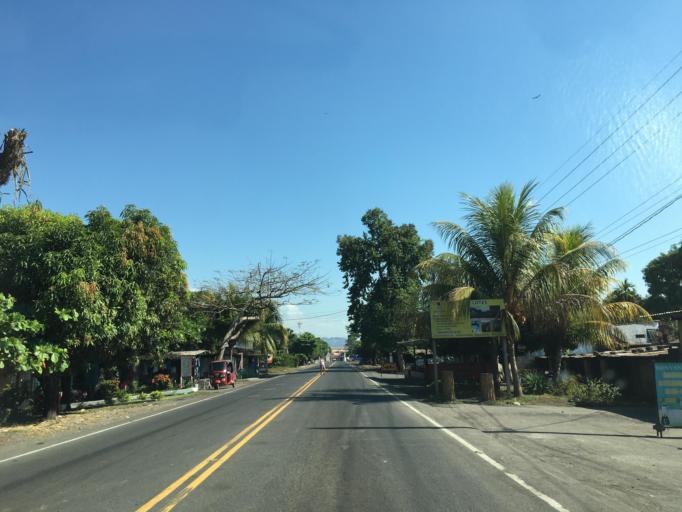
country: GT
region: Escuintla
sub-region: Municipio de La Democracia
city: La Democracia
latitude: 14.2237
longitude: -90.9502
